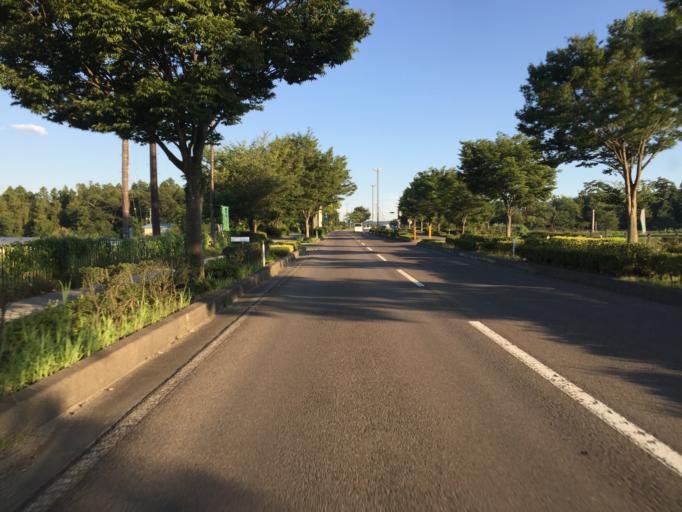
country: JP
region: Fukushima
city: Fukushima-shi
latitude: 37.7380
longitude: 140.3841
